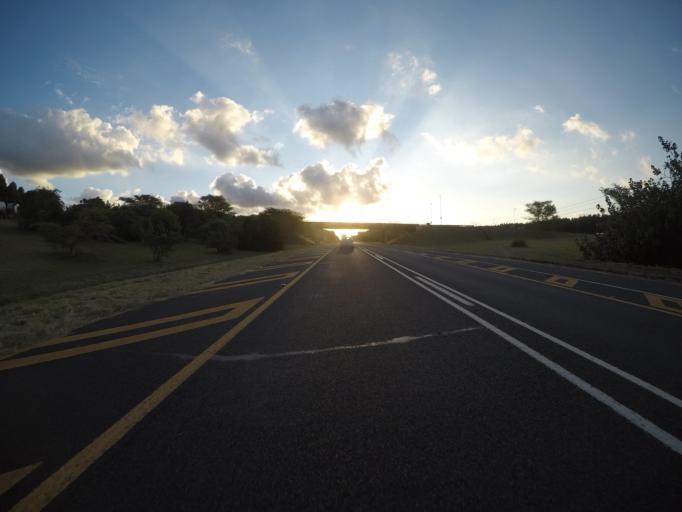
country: ZA
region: KwaZulu-Natal
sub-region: uThungulu District Municipality
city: Richards Bay
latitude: -28.6938
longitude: 32.0300
